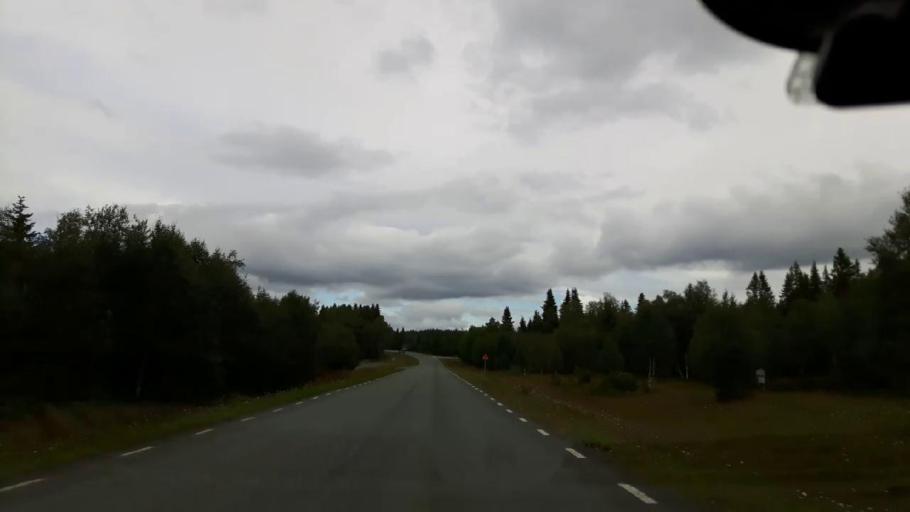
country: SE
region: Jaemtland
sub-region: Krokoms Kommun
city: Valla
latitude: 63.5671
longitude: 13.8423
